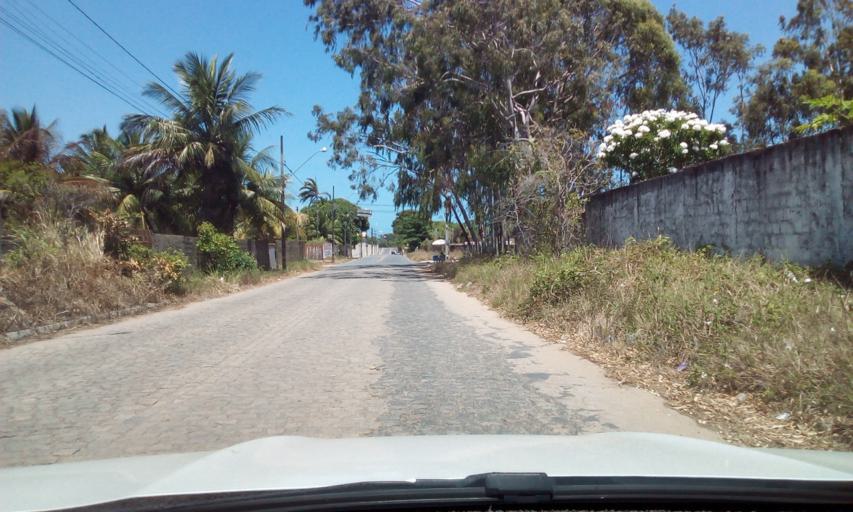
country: BR
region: Paraiba
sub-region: Joao Pessoa
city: Joao Pessoa
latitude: -7.1510
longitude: -34.8093
